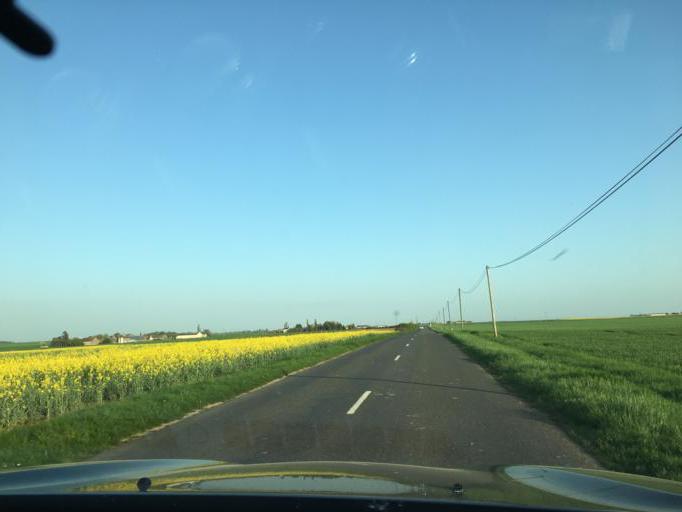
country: FR
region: Centre
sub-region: Departement du Loir-et-Cher
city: Ouzouer-le-Marche
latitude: 47.8489
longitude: 1.5287
